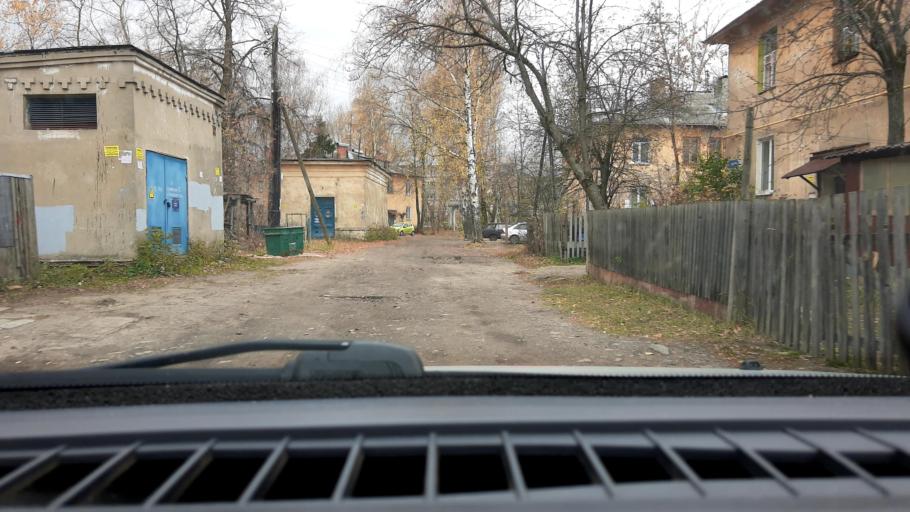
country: RU
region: Nizjnij Novgorod
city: Gorbatovka
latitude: 56.3430
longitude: 43.8254
